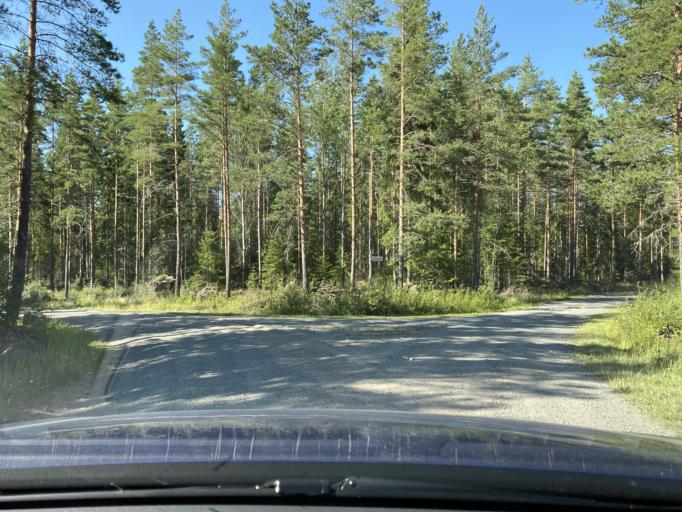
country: FI
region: Satakunta
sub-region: Rauma
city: Kiukainen
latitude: 61.1454
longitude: 22.0212
